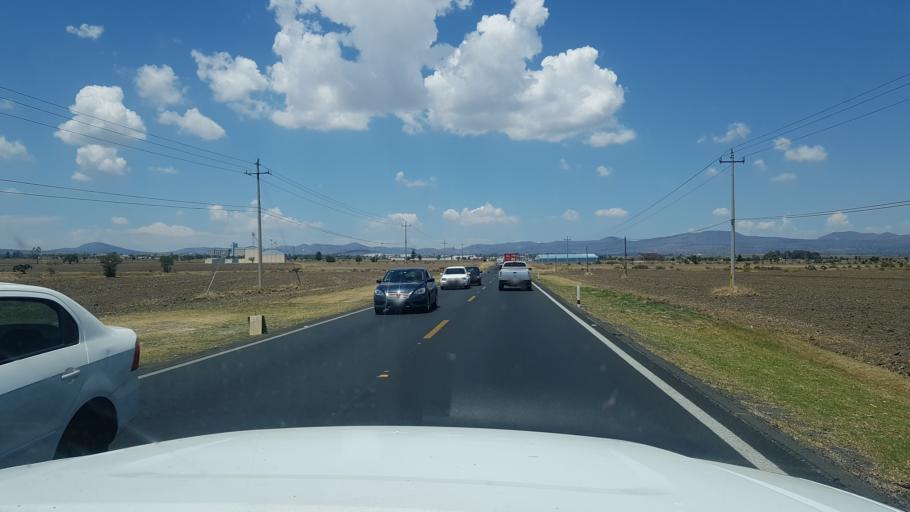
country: MX
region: Hidalgo
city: Calpulalpan
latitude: 19.5777
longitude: -98.5208
